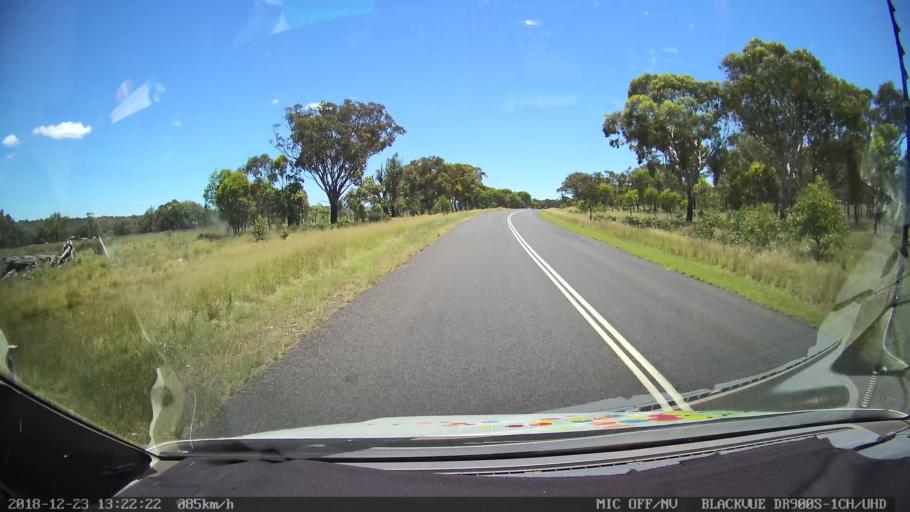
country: AU
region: New South Wales
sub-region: Armidale Dumaresq
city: Armidale
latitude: -30.4791
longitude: 151.4221
